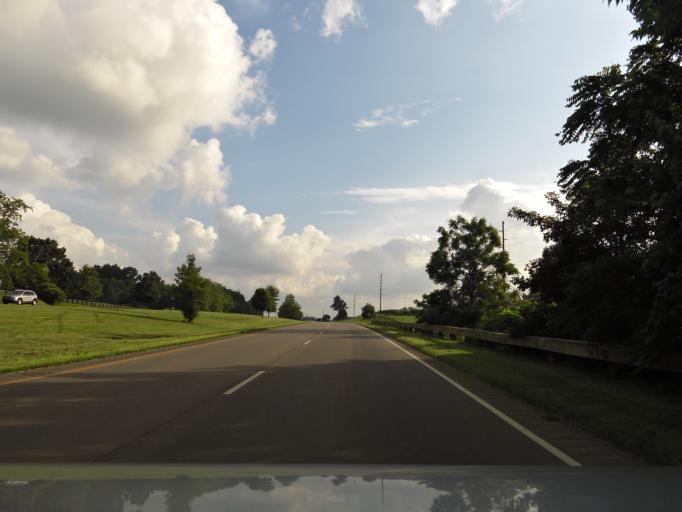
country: US
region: Kentucky
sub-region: Bourbon County
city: Paris
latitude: 38.1761
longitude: -84.3064
